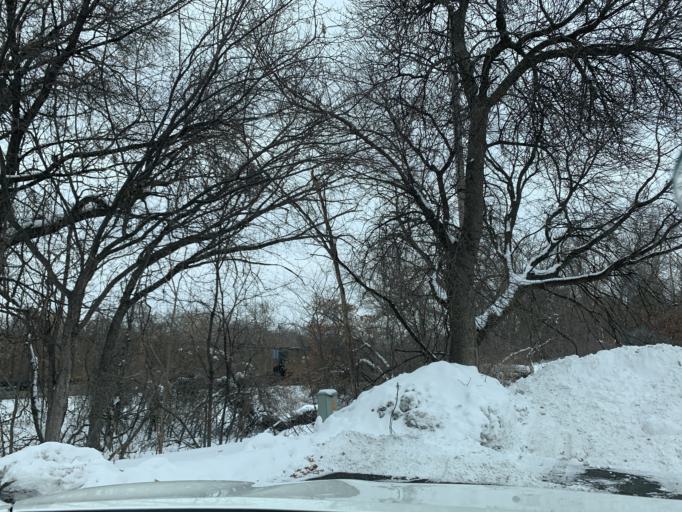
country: US
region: Minnesota
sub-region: Anoka County
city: Coon Rapids
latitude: 45.1676
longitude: -93.2936
